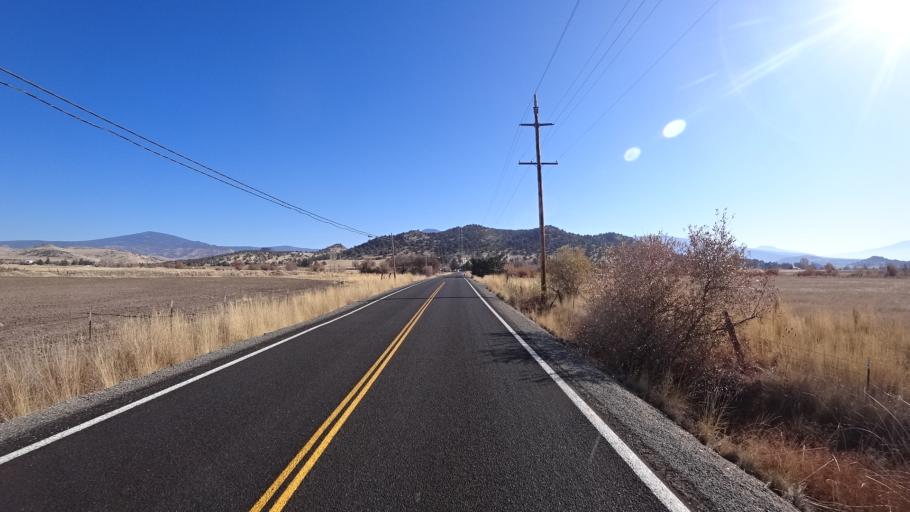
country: US
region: California
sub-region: Siskiyou County
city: Montague
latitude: 41.7115
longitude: -122.3854
